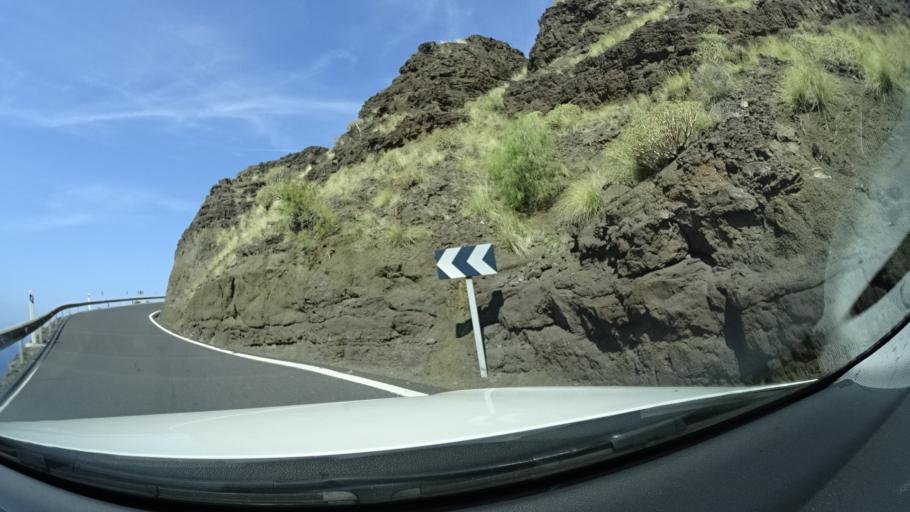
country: ES
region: Canary Islands
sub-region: Provincia de Las Palmas
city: Agaete
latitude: 28.0885
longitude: -15.7034
